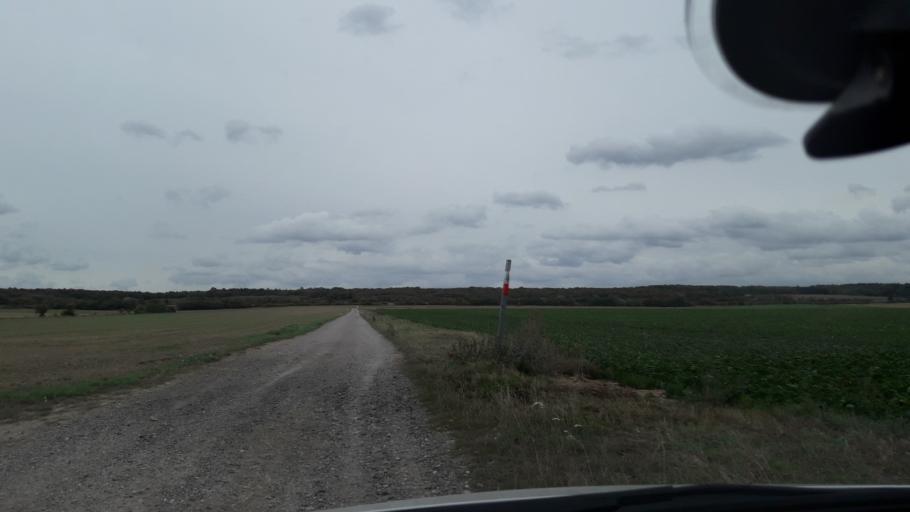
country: DE
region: Lower Saxony
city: Flothe
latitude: 52.0883
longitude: 10.4827
